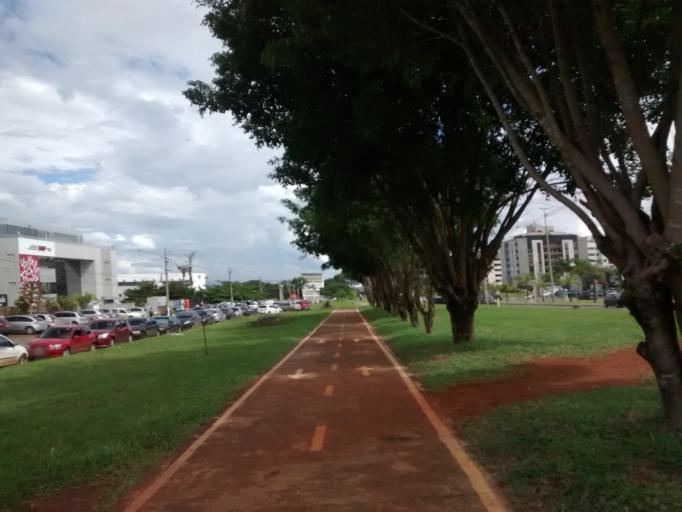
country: BR
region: Federal District
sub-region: Brasilia
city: Brasilia
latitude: -15.7870
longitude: -47.9143
